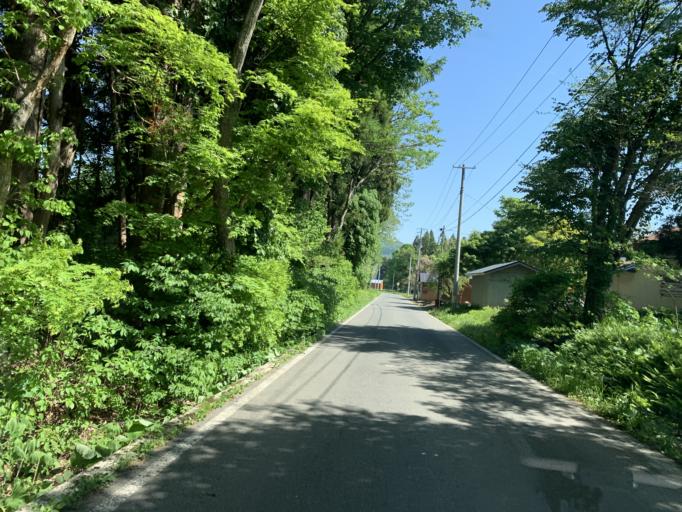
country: JP
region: Iwate
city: Shizukuishi
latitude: 39.5611
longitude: 140.8401
